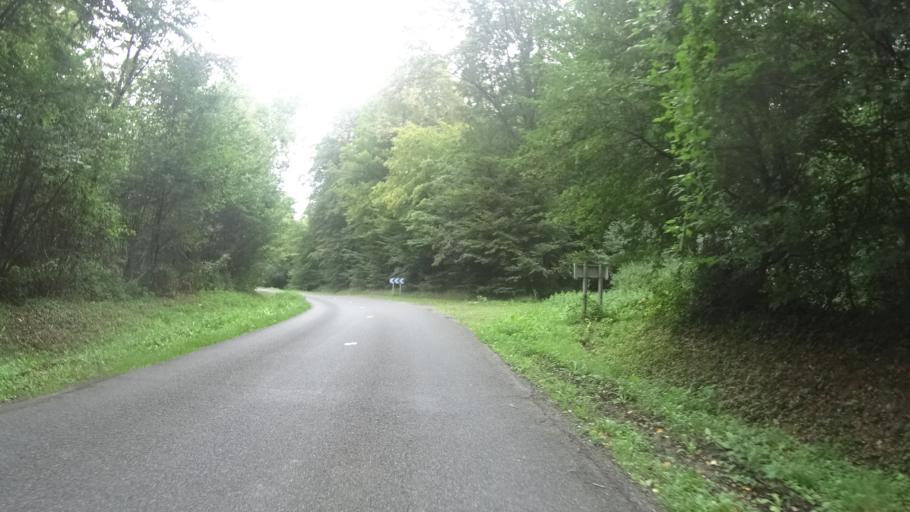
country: FR
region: Picardie
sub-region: Departement de l'Oise
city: Chiry-Ourscamp
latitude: 49.5417
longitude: 2.9813
